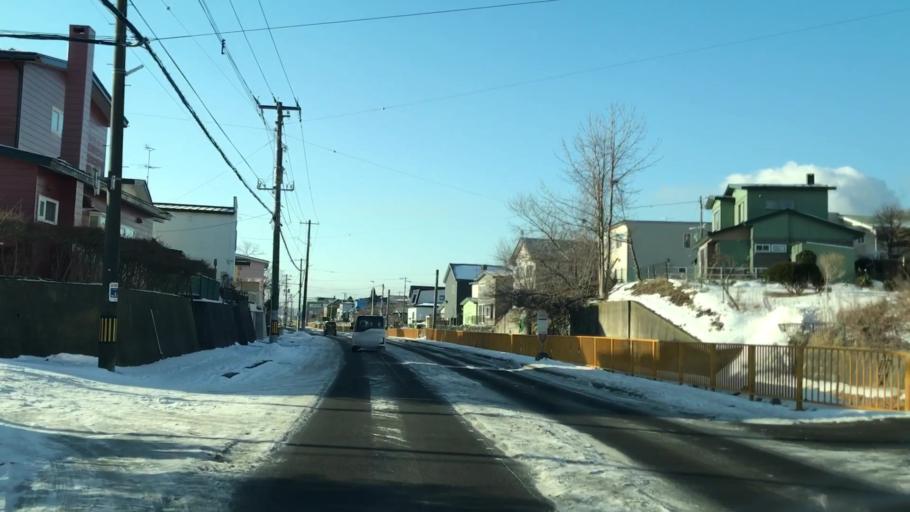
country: JP
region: Hokkaido
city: Muroran
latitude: 42.3694
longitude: 141.0511
